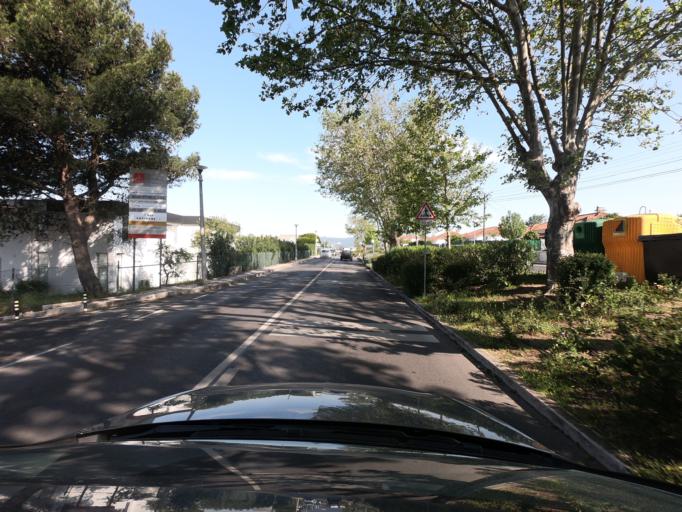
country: PT
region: Lisbon
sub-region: Cascais
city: Parede
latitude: 38.7248
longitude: -9.3528
